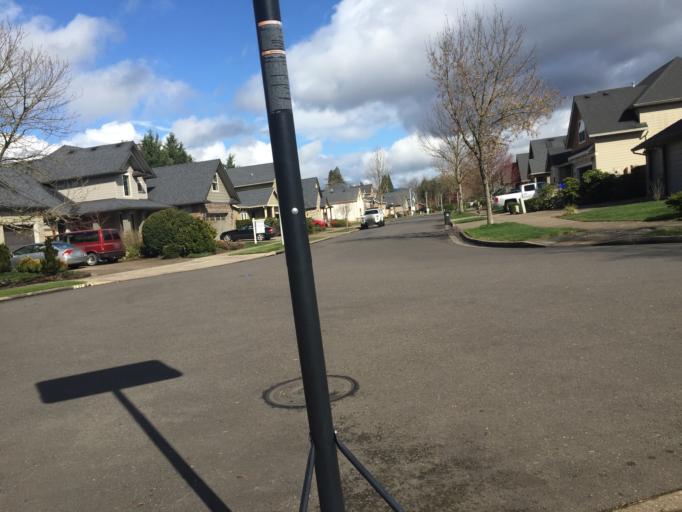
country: US
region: Oregon
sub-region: Lane County
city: Eugene
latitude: 44.1026
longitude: -123.1572
